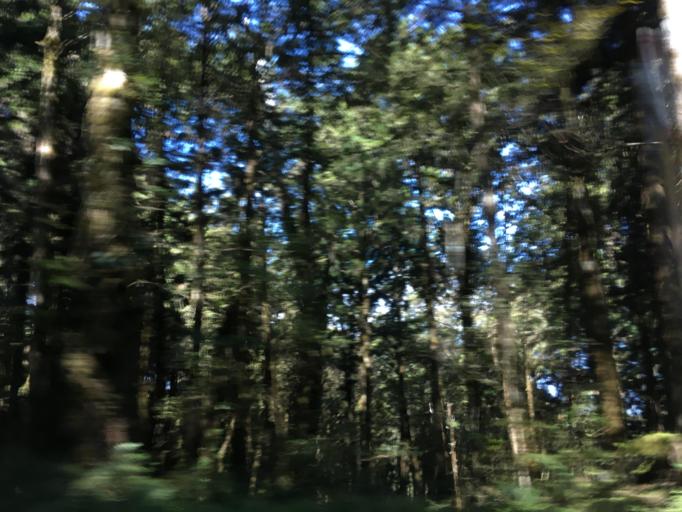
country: TW
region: Taiwan
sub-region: Yilan
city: Yilan
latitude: 24.5159
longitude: 121.5214
